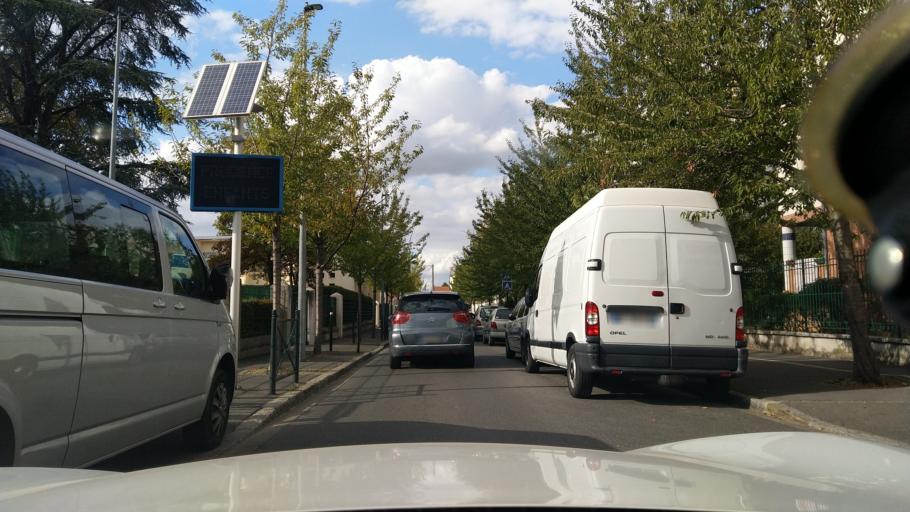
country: FR
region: Ile-de-France
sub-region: Departement de Seine-Saint-Denis
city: Le Blanc-Mesnil
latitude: 48.9253
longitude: 2.4705
